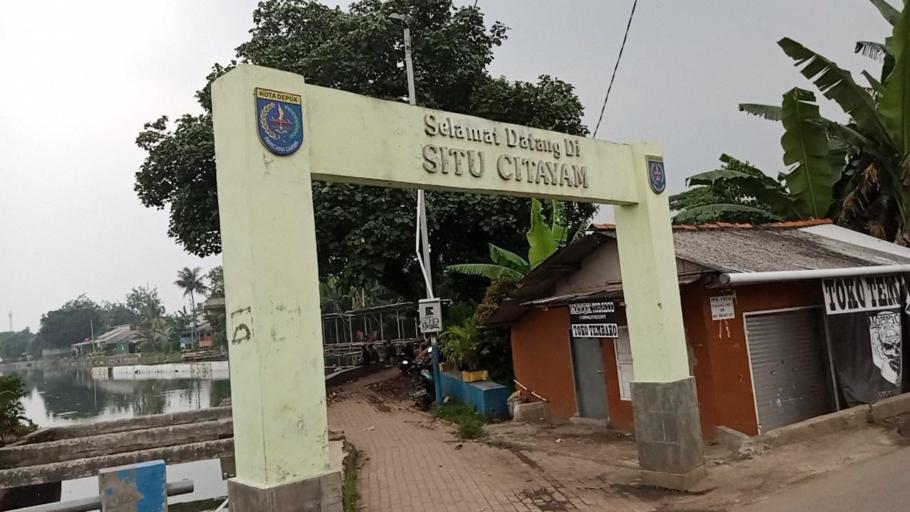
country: ID
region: West Java
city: Depok
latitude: -6.4430
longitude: 106.8001
